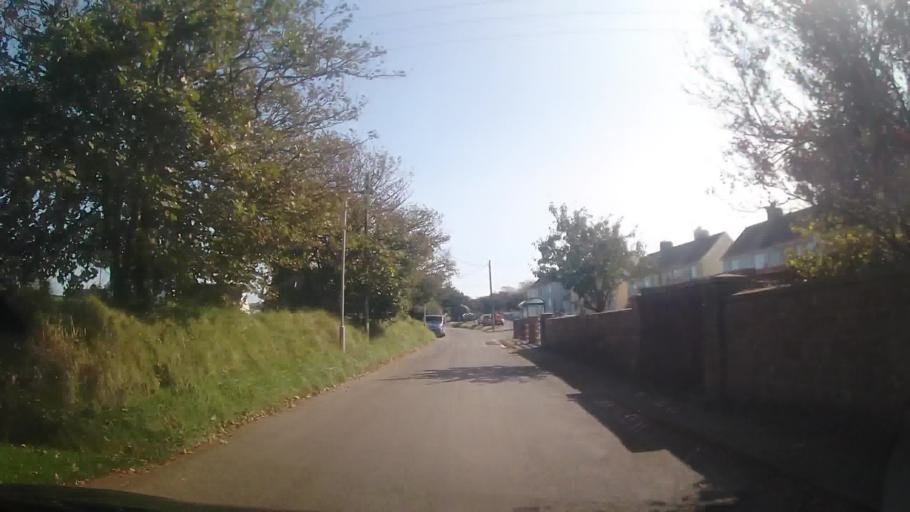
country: GB
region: Wales
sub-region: Pembrokeshire
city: Llanrhian
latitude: 51.9380
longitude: -5.1738
